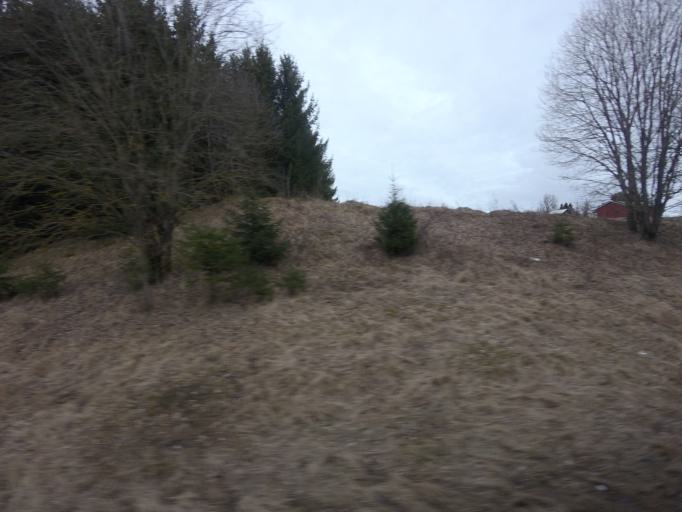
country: NO
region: Ostfold
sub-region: Trogstad
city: Skjonhaug
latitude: 59.6583
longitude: 11.3169
